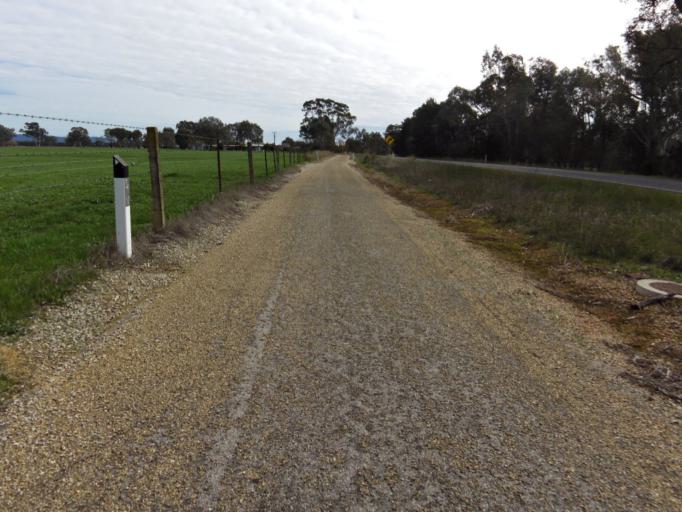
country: AU
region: Victoria
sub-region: Wangaratta
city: Wangaratta
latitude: -36.4080
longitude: 146.3502
